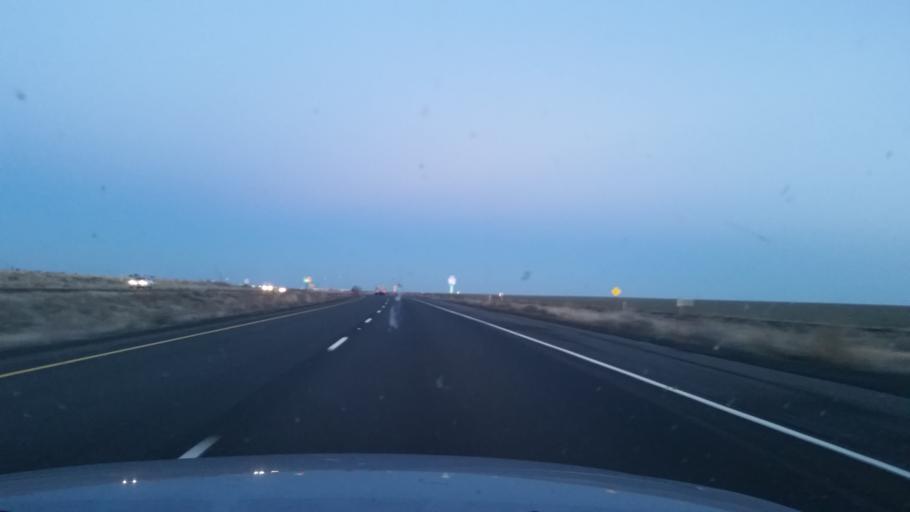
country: US
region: Washington
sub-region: Adams County
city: Ritzville
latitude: 47.1112
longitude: -118.3863
